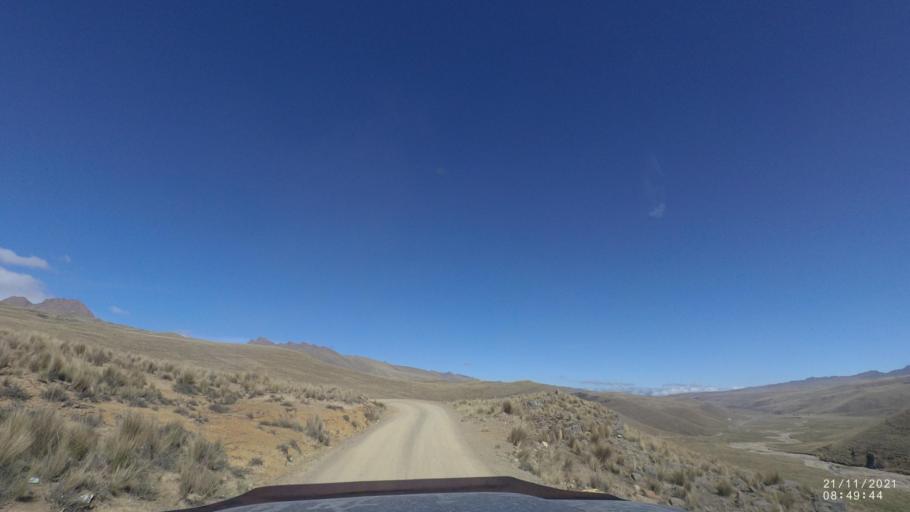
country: BO
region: Cochabamba
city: Cochabamba
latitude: -17.2230
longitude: -66.2330
